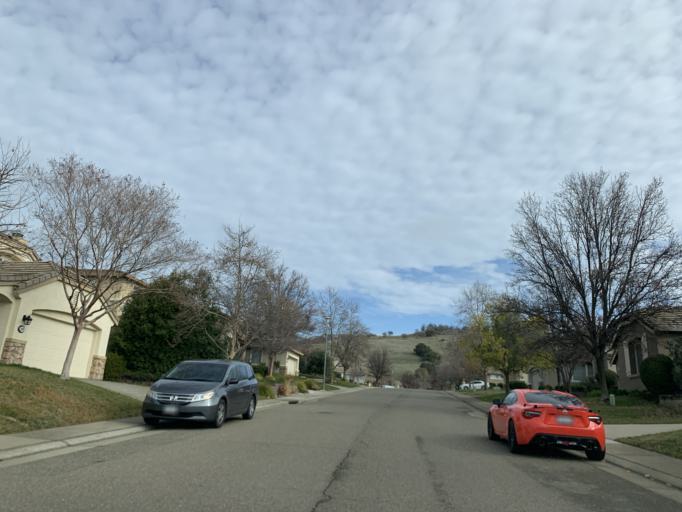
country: US
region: California
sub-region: El Dorado County
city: El Dorado Hills
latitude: 38.6763
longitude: -121.1039
